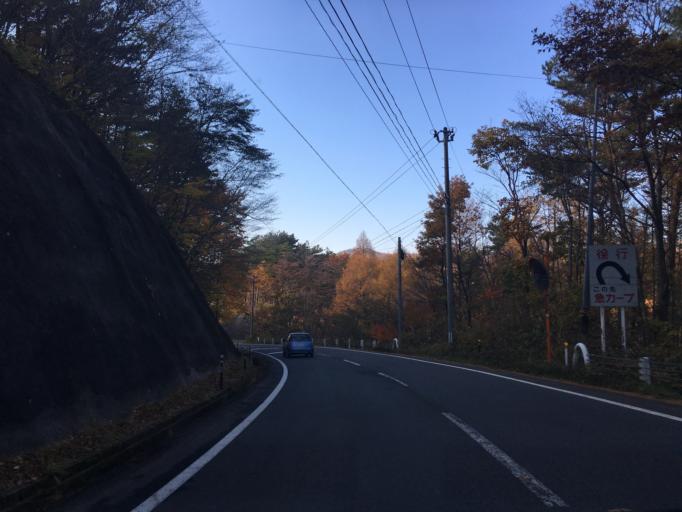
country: JP
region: Fukushima
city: Sukagawa
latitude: 37.2650
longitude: 140.0987
